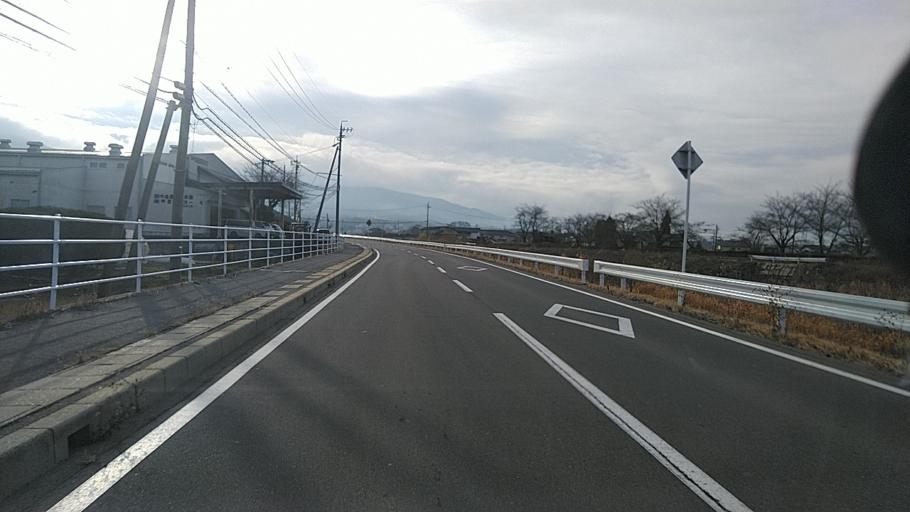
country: JP
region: Nagano
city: Matsumoto
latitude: 36.1938
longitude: 137.9829
